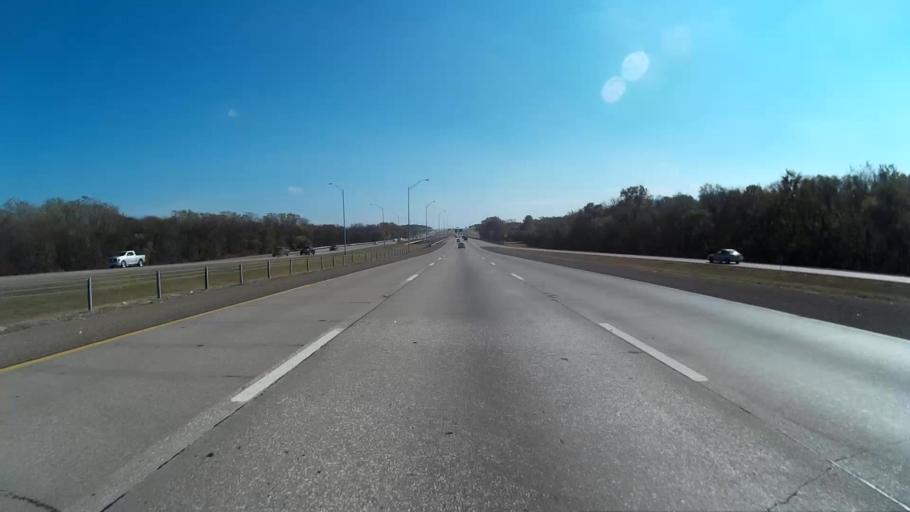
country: US
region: Texas
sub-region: Dallas County
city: Hutchins
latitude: 32.6806
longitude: -96.7435
